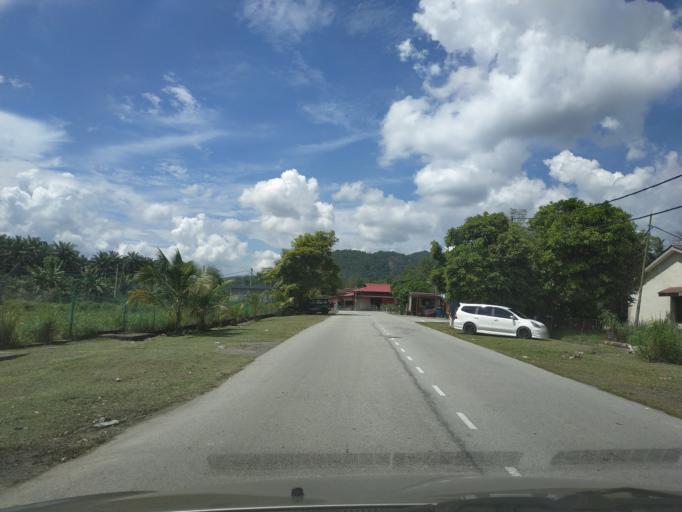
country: MY
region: Perak
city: Parit Buntar
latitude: 5.1384
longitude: 100.5941
